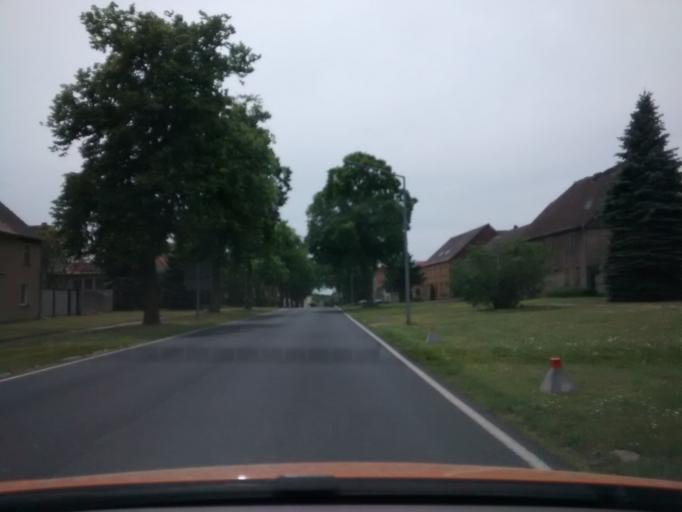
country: DE
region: Brandenburg
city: Juterbog
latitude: 51.9028
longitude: 13.1409
